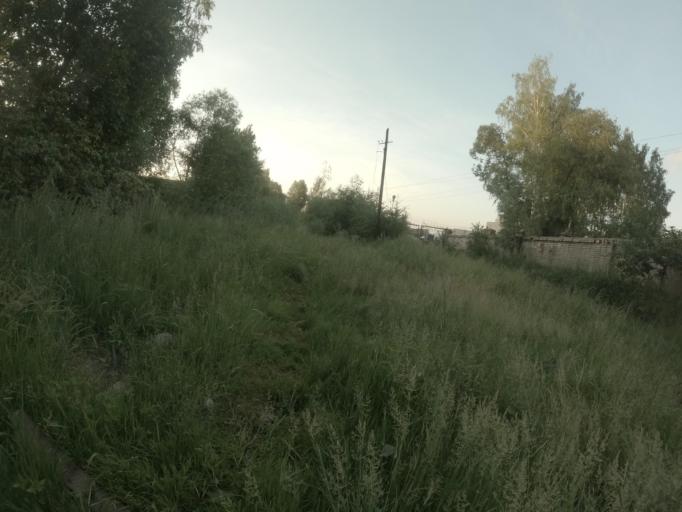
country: RU
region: St.-Petersburg
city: Krasnogvargeisky
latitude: 59.9442
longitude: 30.4405
